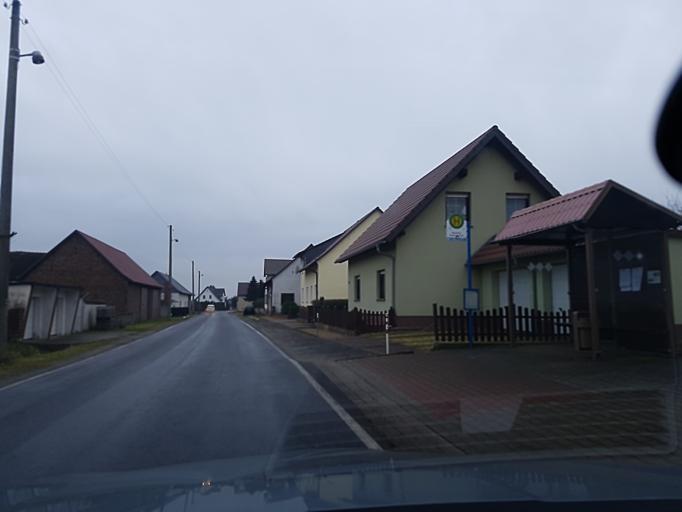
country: DE
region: Brandenburg
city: Schilda
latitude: 51.6463
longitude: 13.3877
